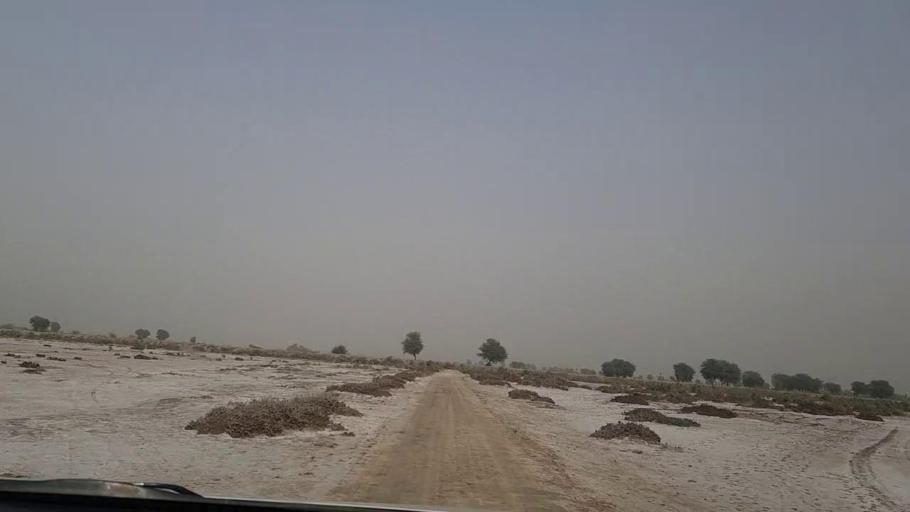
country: PK
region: Sindh
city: Pithoro
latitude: 25.4691
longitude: 69.2705
